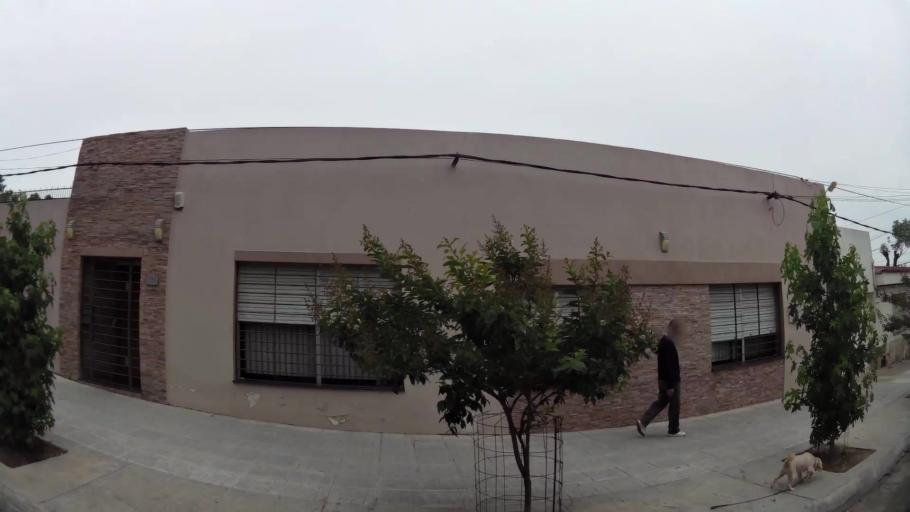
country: UY
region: Canelones
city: Las Piedras
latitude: -34.7244
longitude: -56.2202
